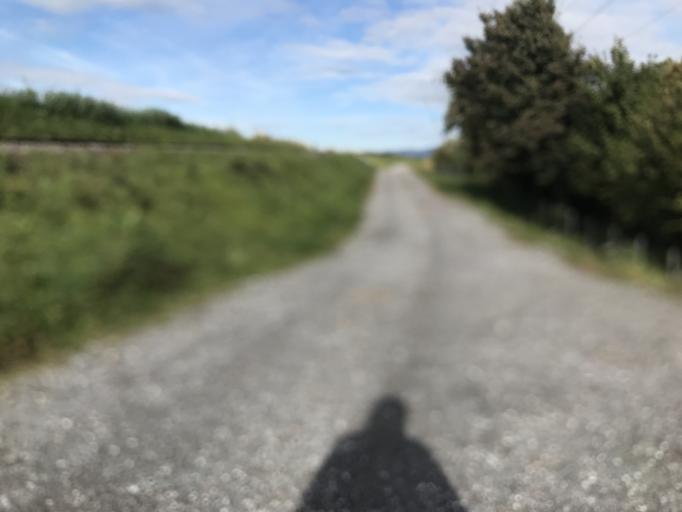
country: AT
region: Vorarlberg
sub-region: Politischer Bezirk Feldkirch
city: Mader
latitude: 47.3484
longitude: 9.6044
